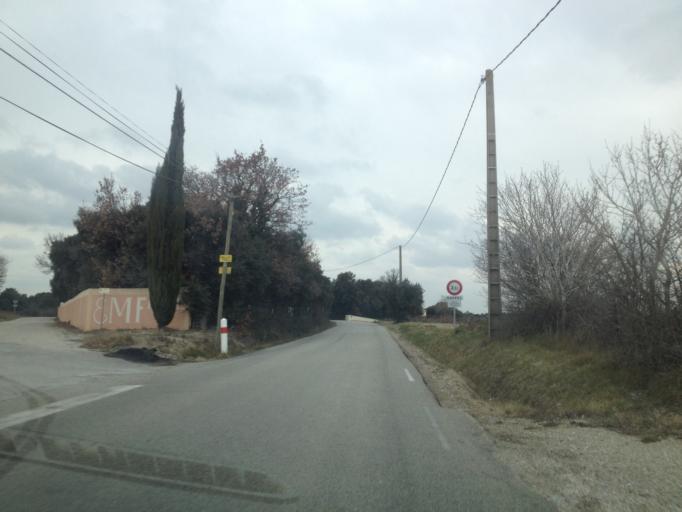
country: FR
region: Provence-Alpes-Cote d'Azur
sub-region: Departement du Vaucluse
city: Courthezon
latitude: 44.1062
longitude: 4.8766
